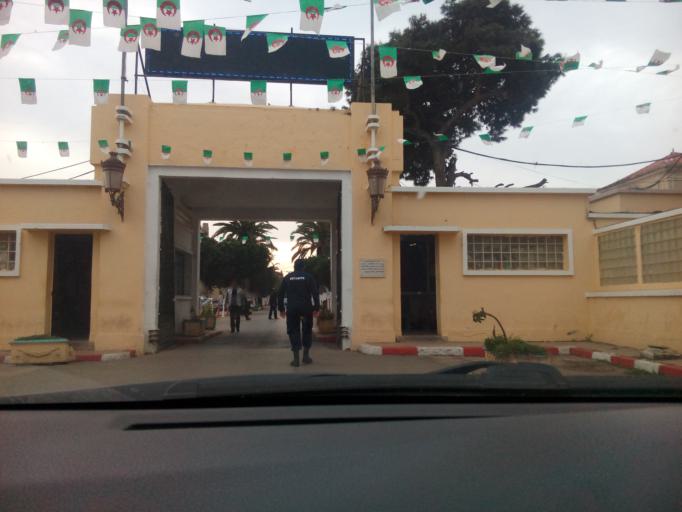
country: DZ
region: Oran
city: Oran
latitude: 35.6951
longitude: -0.6424
